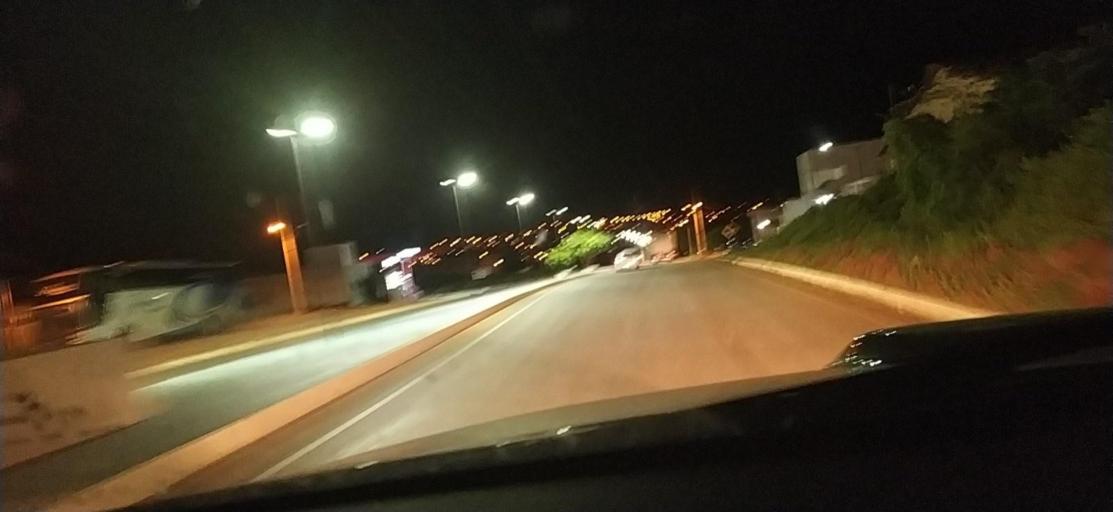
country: BR
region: Minas Gerais
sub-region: Monte Azul
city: Monte Azul
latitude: -15.1597
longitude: -42.8670
